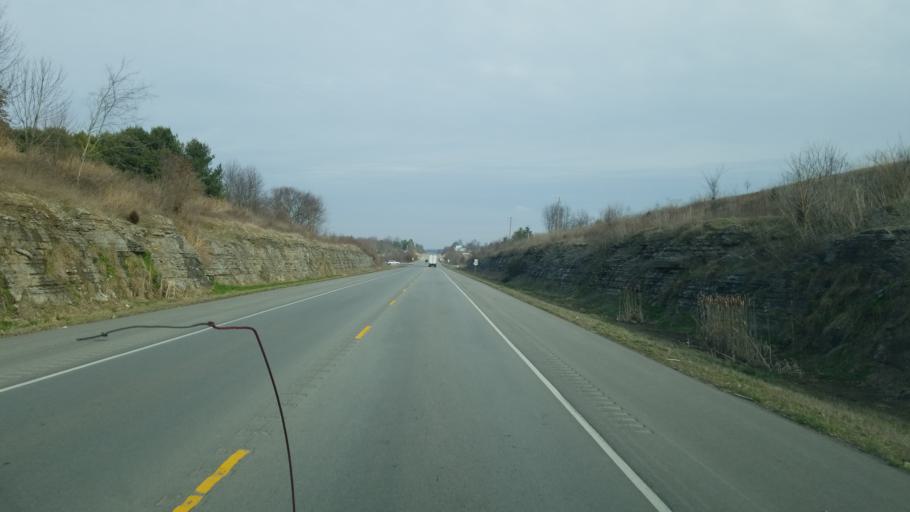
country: US
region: Kentucky
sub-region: Boyle County
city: Junction City
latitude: 37.5354
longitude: -84.8043
